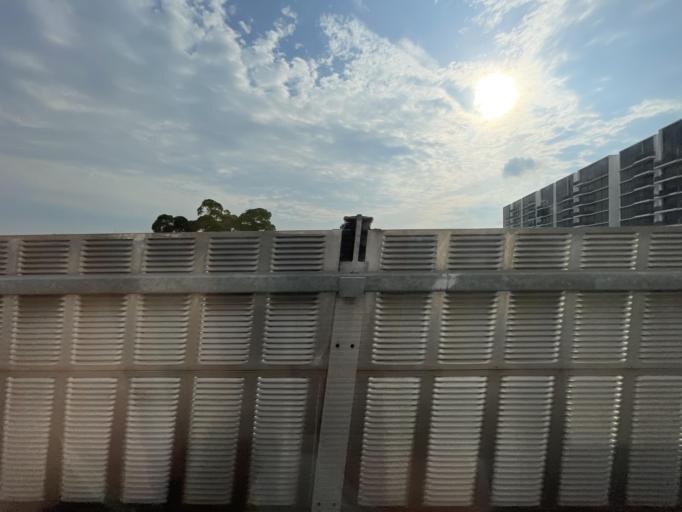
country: SG
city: Singapore
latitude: 1.3413
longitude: 103.9549
